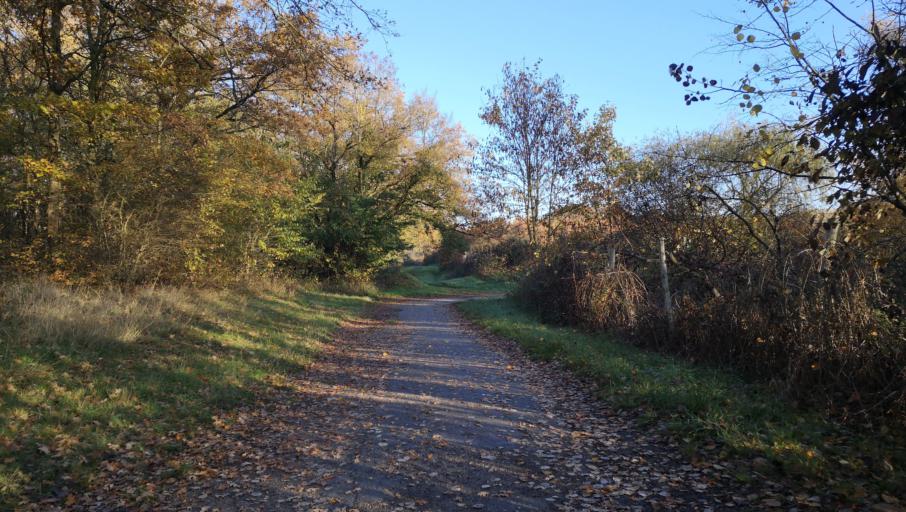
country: FR
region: Centre
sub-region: Departement du Loiret
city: Saran
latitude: 47.9415
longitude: 1.8614
